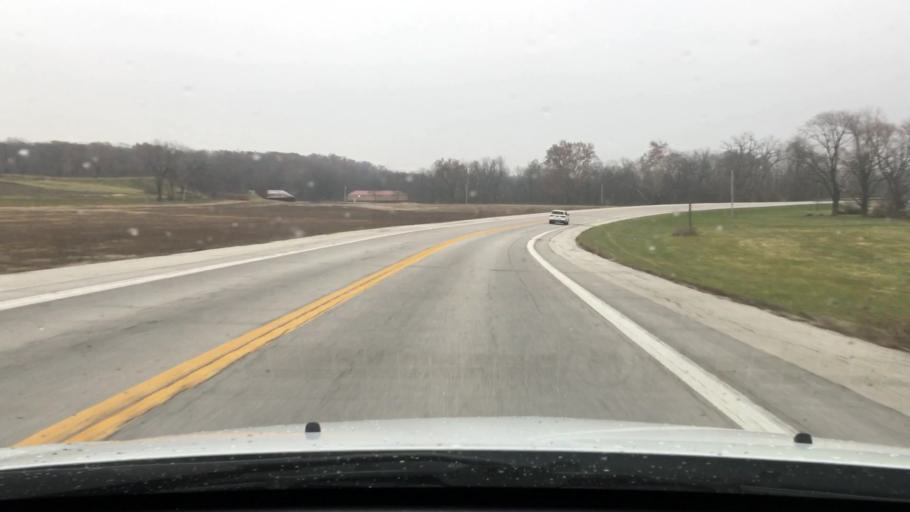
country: US
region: Missouri
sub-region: Pike County
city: Bowling Green
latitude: 39.3787
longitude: -91.1519
